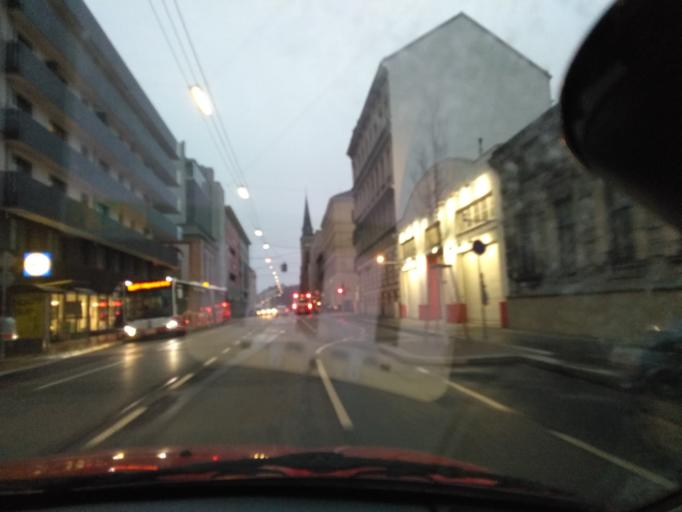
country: AT
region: Vienna
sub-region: Wien Stadt
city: Vienna
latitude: 48.2168
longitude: 16.3197
